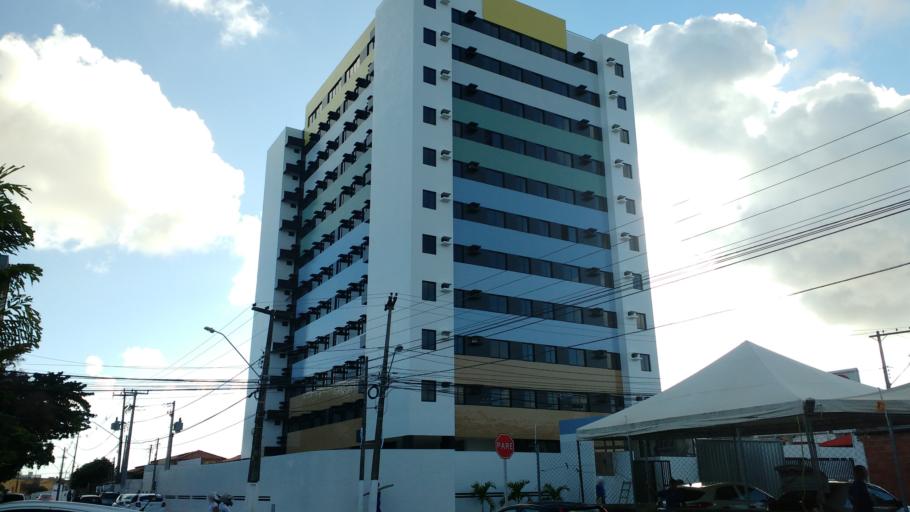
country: BR
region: Alagoas
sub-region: Maceio
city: Maceio
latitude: -9.6335
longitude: -35.7393
